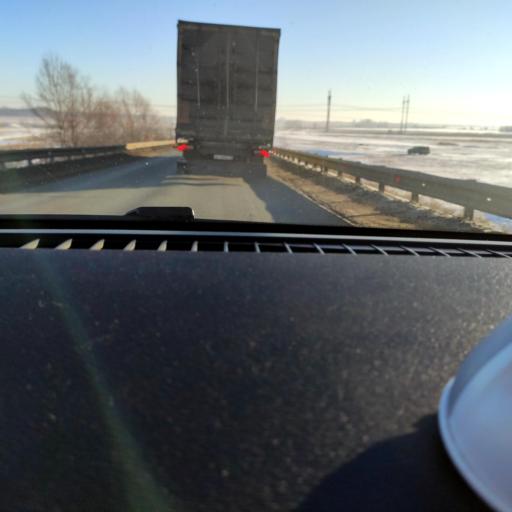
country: RU
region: Samara
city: Spiridonovka
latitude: 53.1431
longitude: 50.5899
